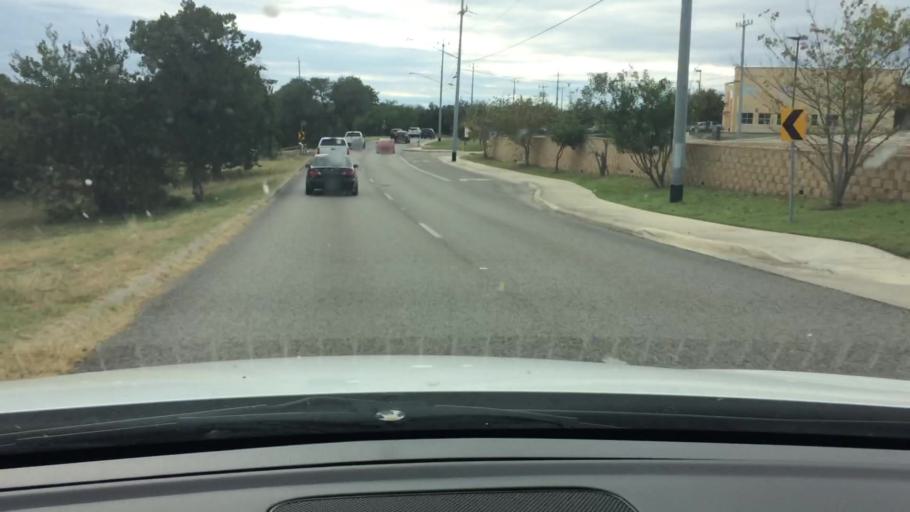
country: US
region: Texas
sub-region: Bexar County
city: Hollywood Park
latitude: 29.6365
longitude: -98.4482
